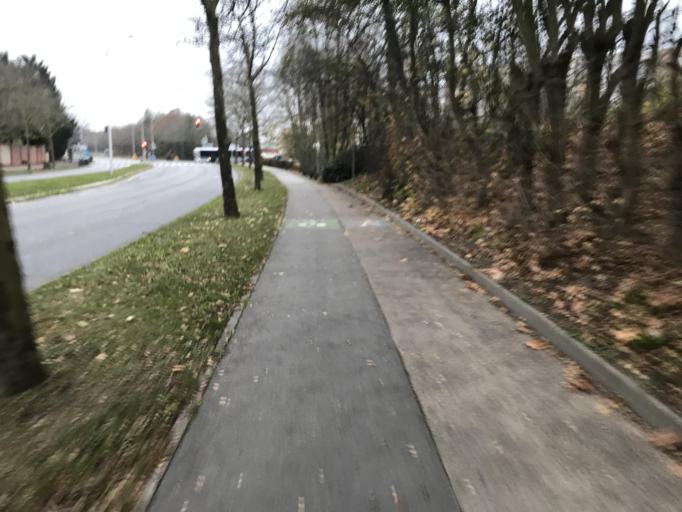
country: FR
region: Ile-de-France
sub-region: Departement des Yvelines
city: Saint-Quentin-en-Yvelines
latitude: 48.7675
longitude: 2.0191
